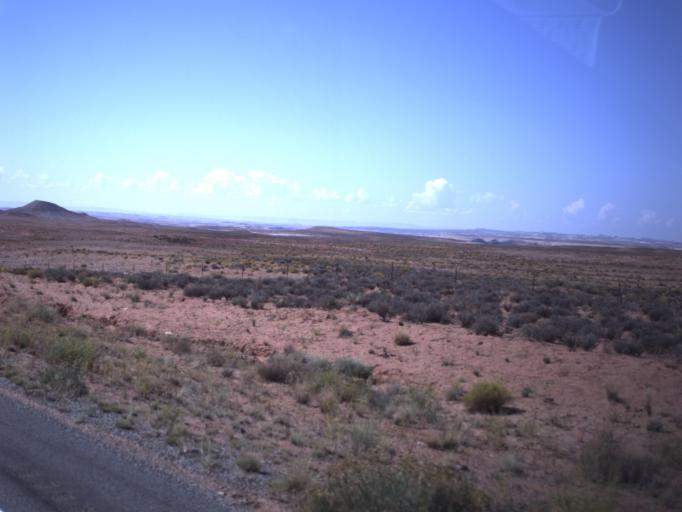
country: US
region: Utah
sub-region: San Juan County
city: Blanding
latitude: 37.0138
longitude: -109.6122
